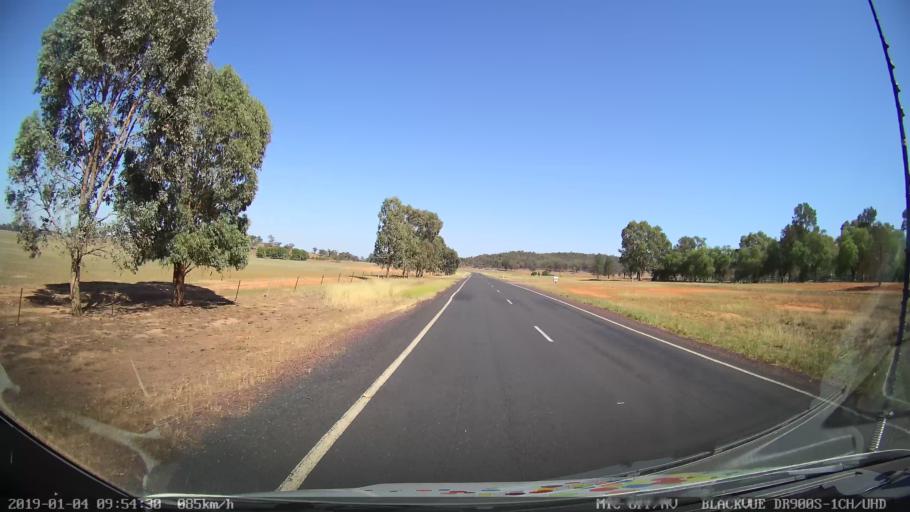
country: AU
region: New South Wales
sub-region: Cabonne
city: Canowindra
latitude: -33.5407
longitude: 148.4140
